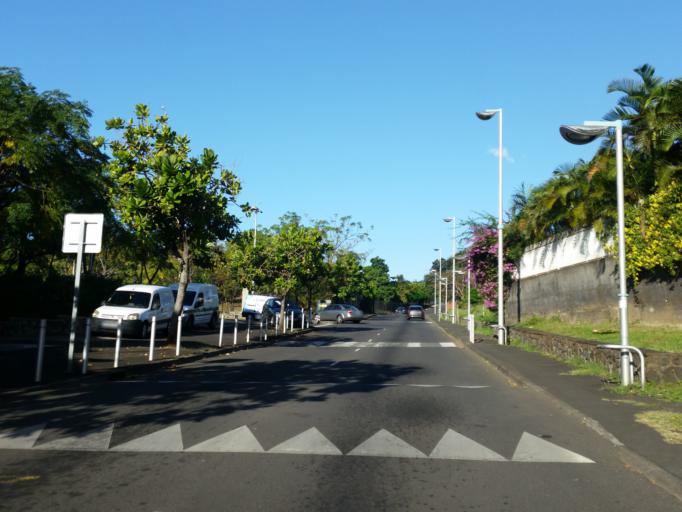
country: RE
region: Reunion
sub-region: Reunion
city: Saint-Denis
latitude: -20.8970
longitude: 55.4699
